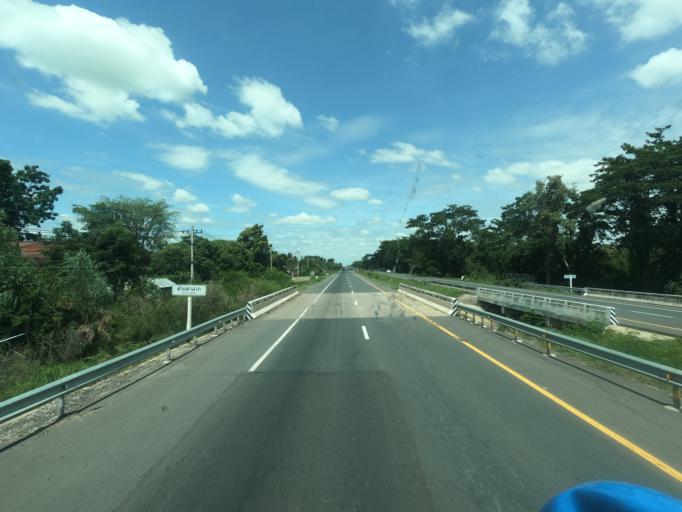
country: TH
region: Surin
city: Prasat
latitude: 14.6196
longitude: 103.3668
